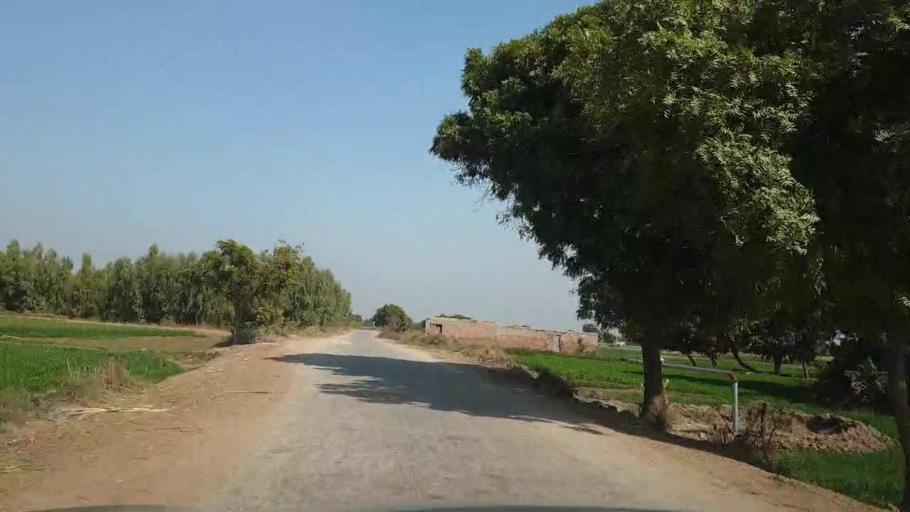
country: PK
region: Sindh
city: Tando Allahyar
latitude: 25.5719
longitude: 68.7205
